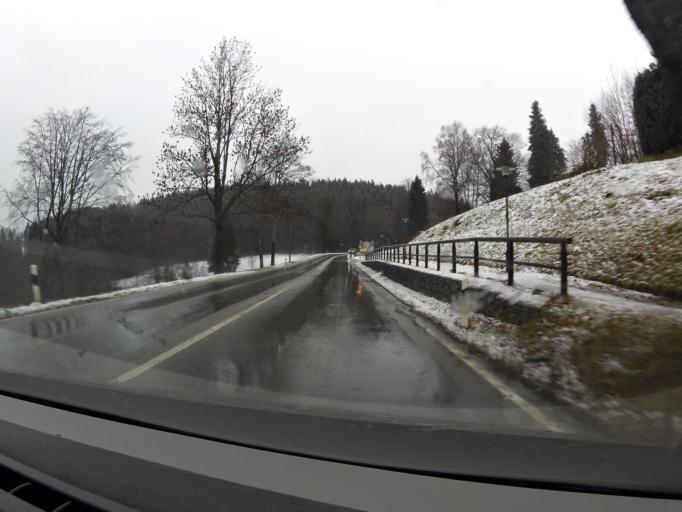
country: DE
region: Bavaria
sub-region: Upper Bavaria
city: Bad Wiessee
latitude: 47.7253
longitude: 11.7179
